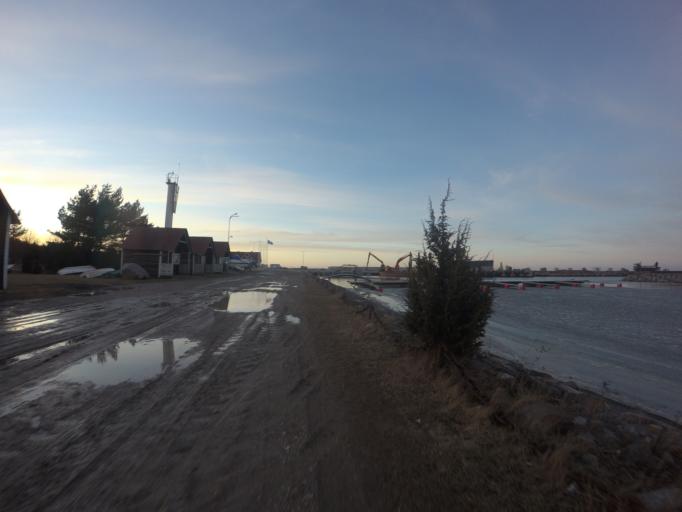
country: EE
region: Saare
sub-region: Orissaare vald
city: Orissaare
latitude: 58.5909
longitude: 22.7182
